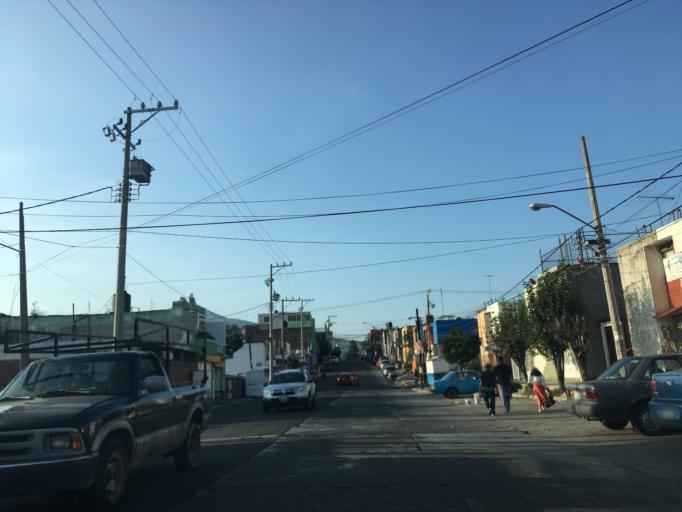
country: MX
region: Michoacan
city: Morelia
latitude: 19.7003
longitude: -101.2289
